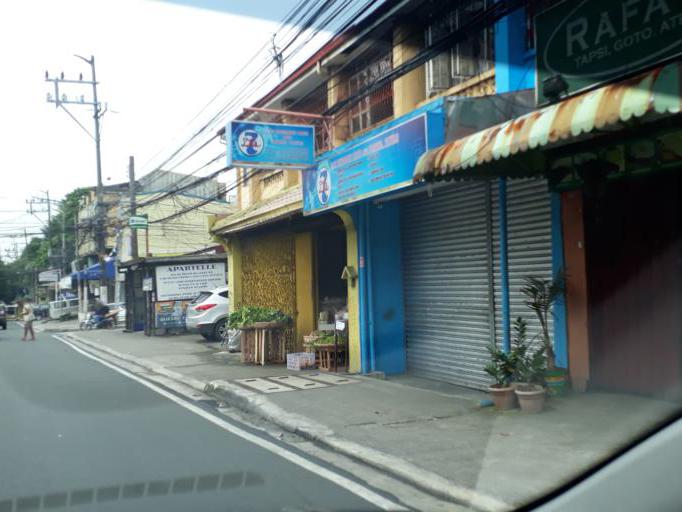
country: PH
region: Metro Manila
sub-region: Quezon City
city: Quezon City
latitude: 14.6311
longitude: 121.0390
